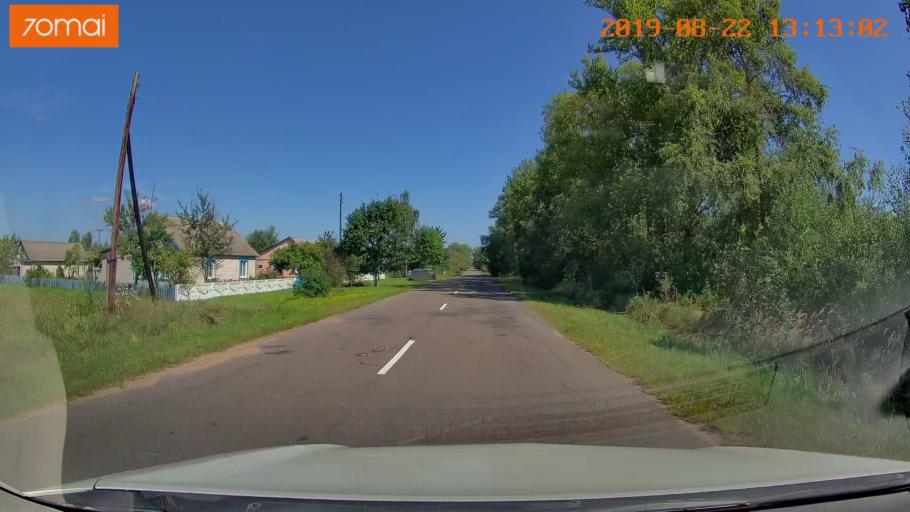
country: BY
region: Minsk
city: Prawdzinski
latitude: 53.2691
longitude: 27.8710
